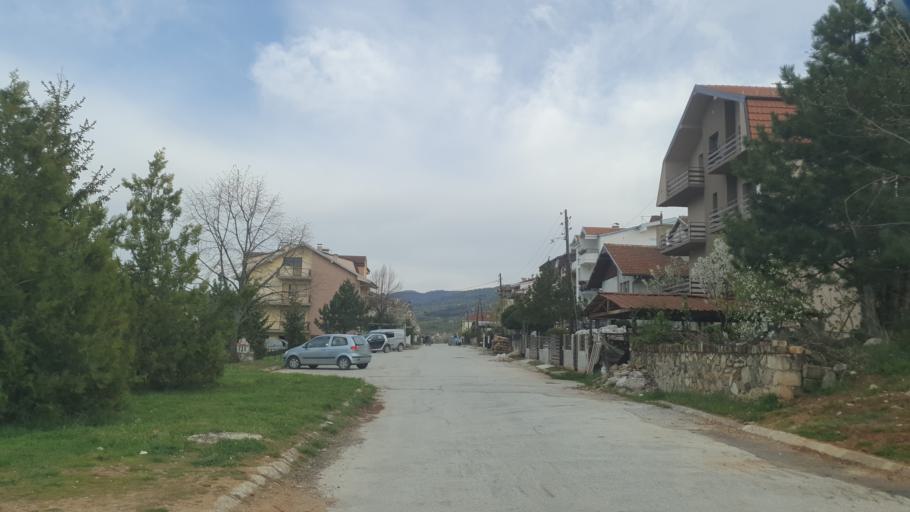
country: MK
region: Bitola
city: Bitola
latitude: 41.0307
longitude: 21.3001
